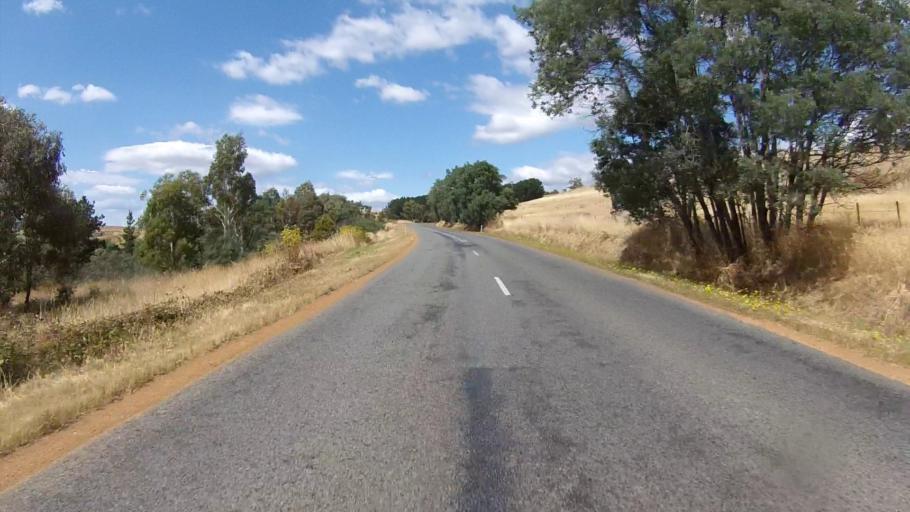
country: AU
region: Tasmania
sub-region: Derwent Valley
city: New Norfolk
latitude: -42.6864
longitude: 146.8701
